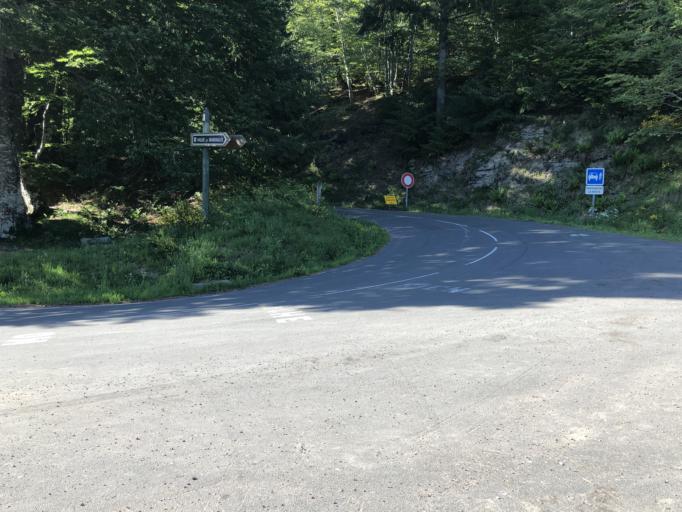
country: FR
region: Auvergne
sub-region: Departement du Cantal
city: Vic-sur-Cere
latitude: 45.0923
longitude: 2.6932
